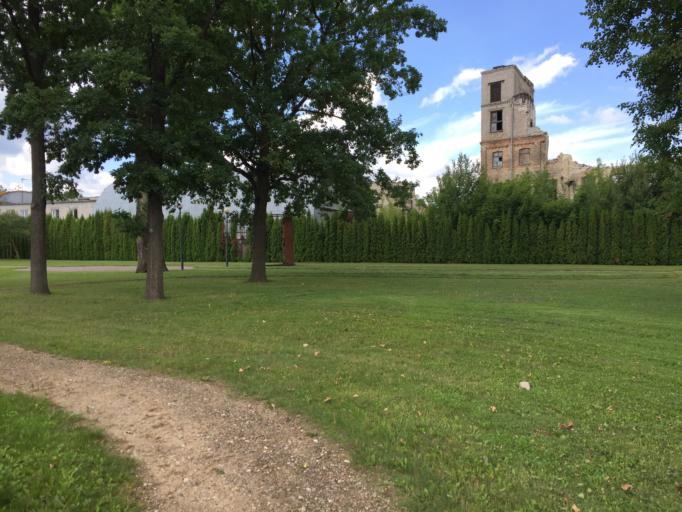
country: LV
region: Jelgava
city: Jelgava
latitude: 56.6594
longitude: 23.7180
